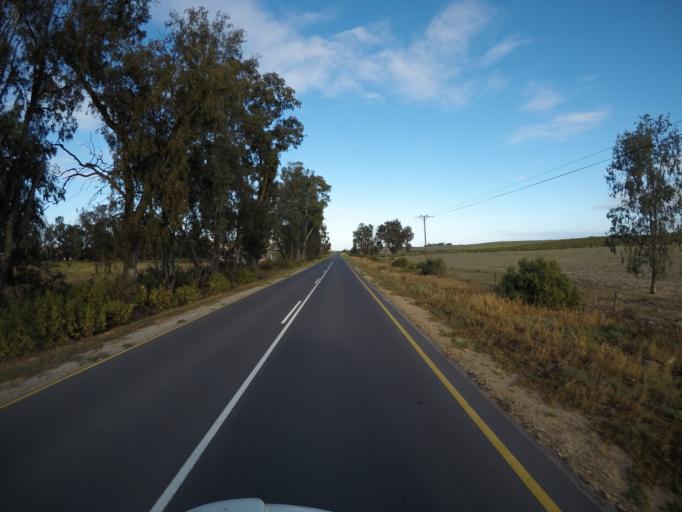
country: ZA
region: Western Cape
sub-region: West Coast District Municipality
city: Clanwilliam
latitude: -32.3115
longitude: 18.3797
